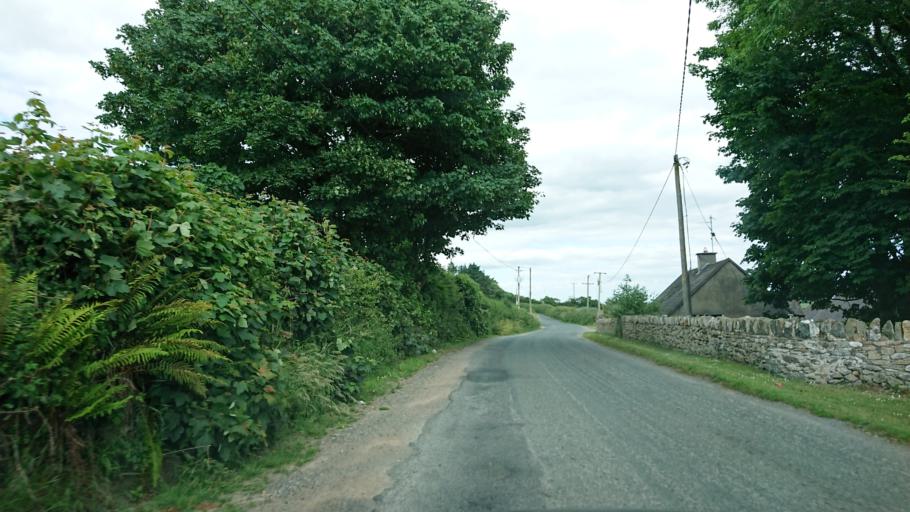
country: IE
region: Munster
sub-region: Waterford
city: Tra Mhor
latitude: 52.1991
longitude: -7.1916
